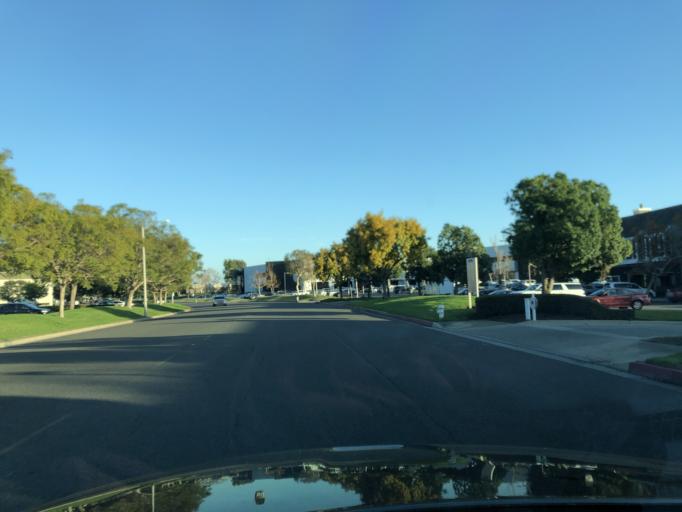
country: US
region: California
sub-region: Orange County
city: Costa Mesa
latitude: 33.6725
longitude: -117.8815
